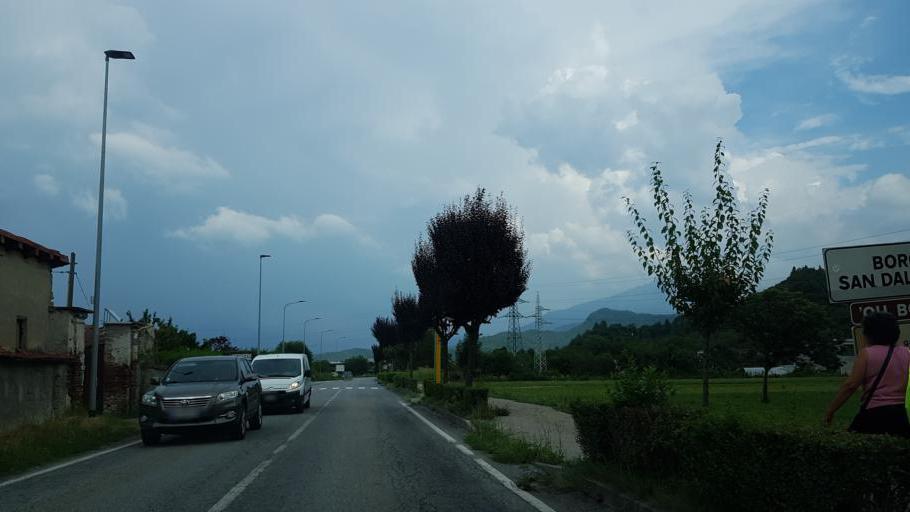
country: IT
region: Piedmont
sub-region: Provincia di Cuneo
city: Roccasparvera
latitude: 44.3344
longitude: 7.4646
